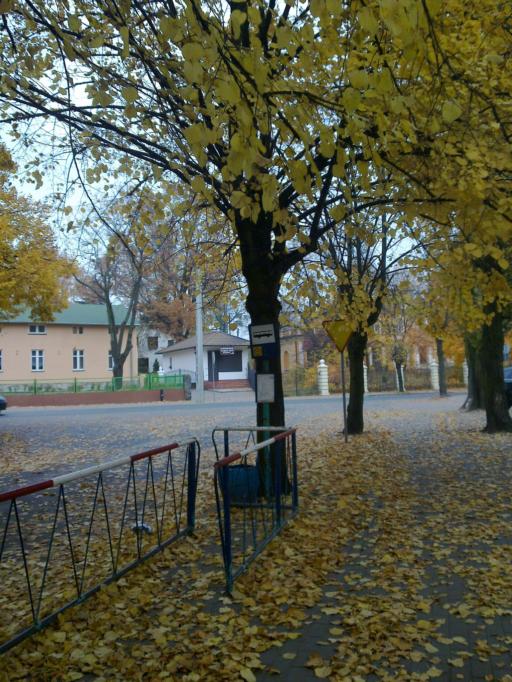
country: PL
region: Kujawsko-Pomorskie
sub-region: Powiat aleksandrowski
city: Aleksandrow Kujawski
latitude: 52.8756
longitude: 18.6980
